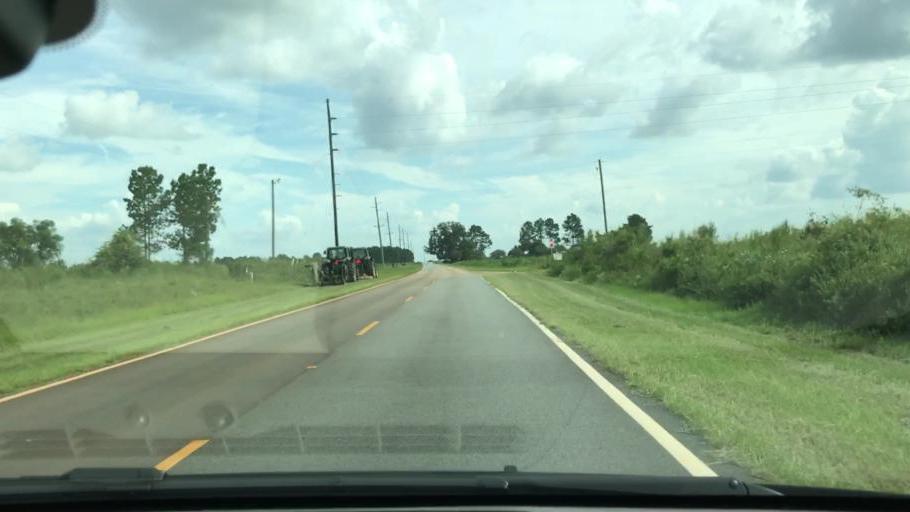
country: US
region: Georgia
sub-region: Clay County
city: Fort Gaines
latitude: 31.5403
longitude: -84.9621
